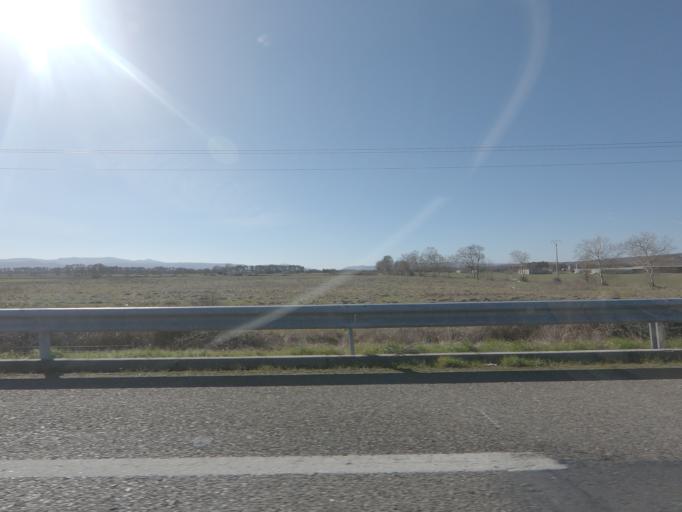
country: ES
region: Galicia
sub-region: Provincia de Ourense
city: Xinzo de Limia
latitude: 42.0957
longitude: -7.7267
